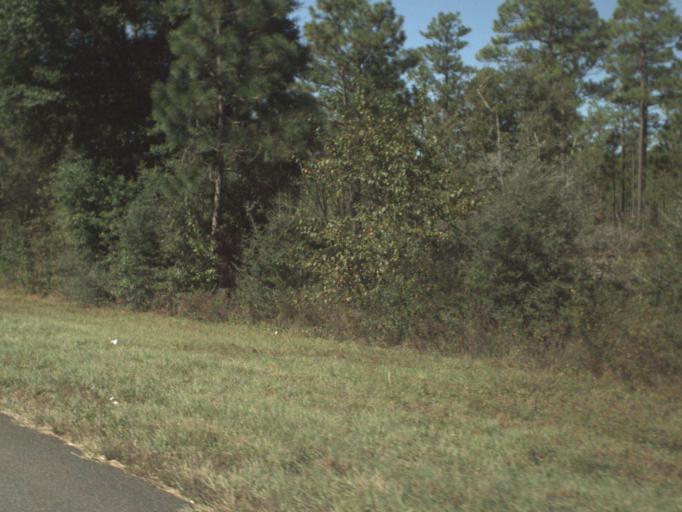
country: US
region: Florida
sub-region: Santa Rosa County
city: East Milton
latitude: 30.6891
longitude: -86.8184
